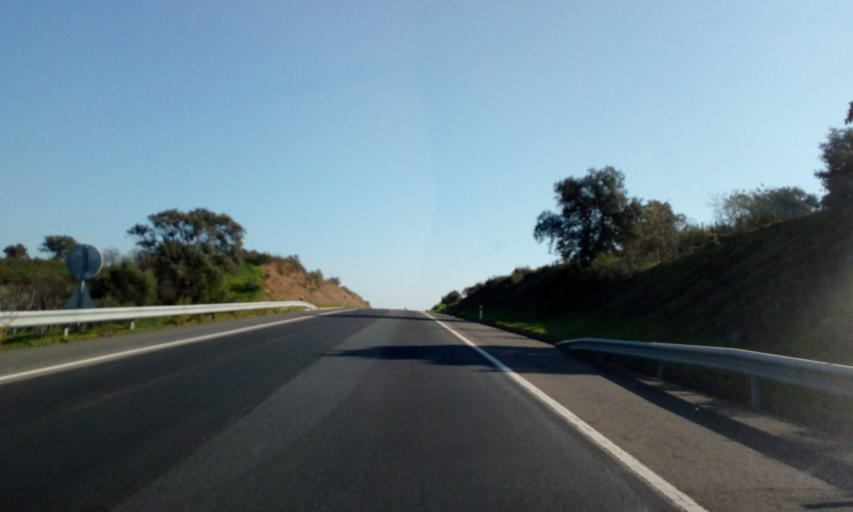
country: PT
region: Faro
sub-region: Castro Marim
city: Castro Marim
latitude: 37.2446
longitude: -7.4652
